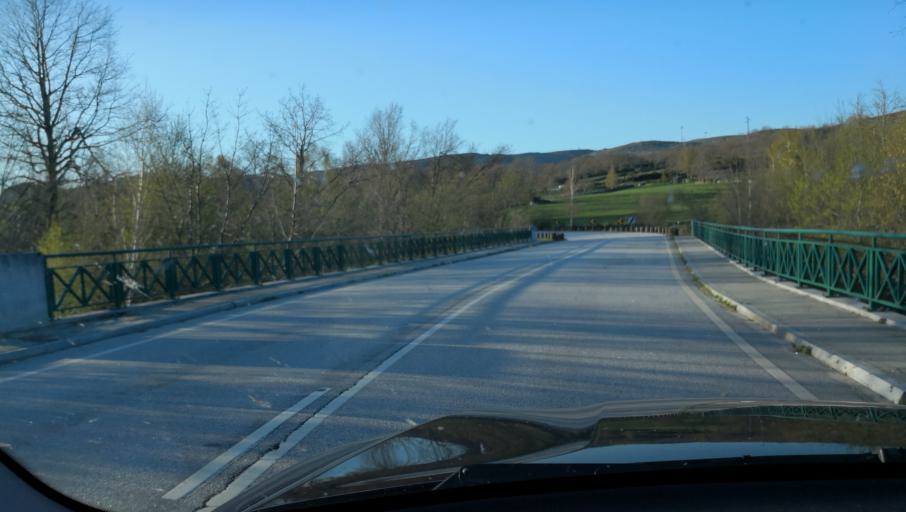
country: PT
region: Vila Real
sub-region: Vila Real
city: Vila Real
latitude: 41.3683
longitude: -7.8013
